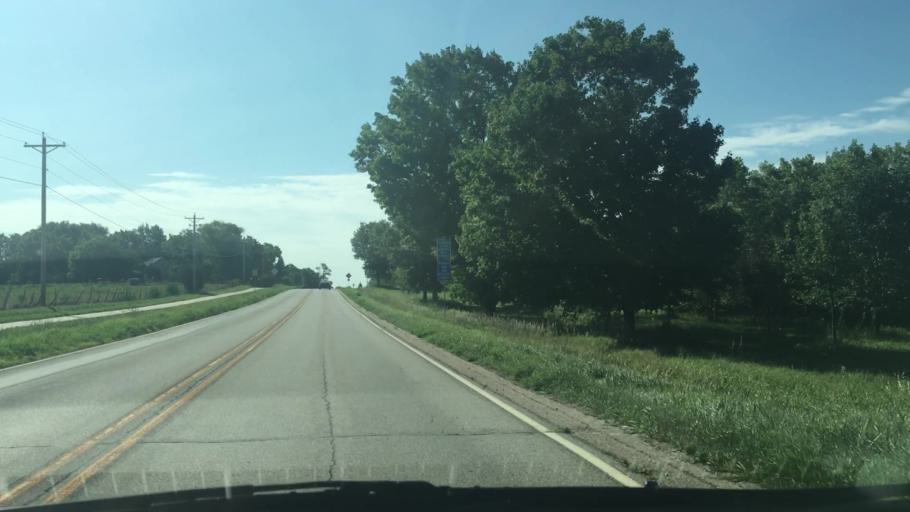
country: US
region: Iowa
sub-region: Johnson County
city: North Liberty
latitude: 41.7327
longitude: -91.5655
